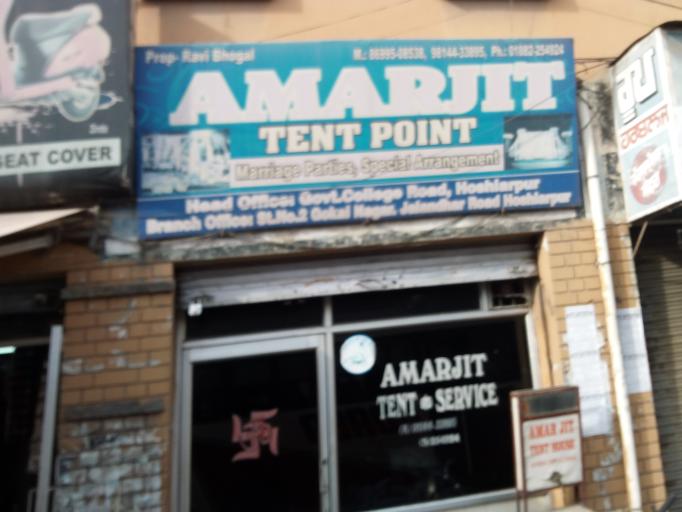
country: IN
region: Punjab
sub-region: Hoshiarpur
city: Hoshiarpur
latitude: 31.5272
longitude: 75.8988
